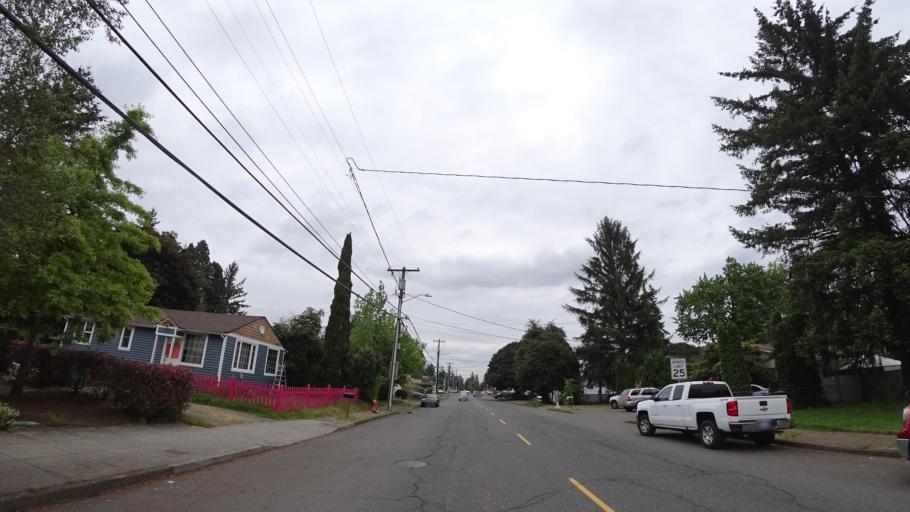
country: US
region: Oregon
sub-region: Multnomah County
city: Lents
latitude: 45.5116
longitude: -122.5398
